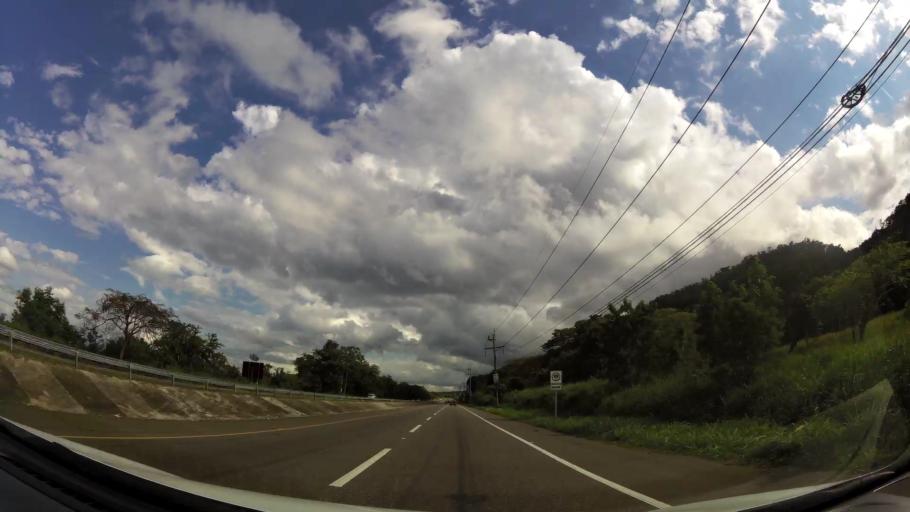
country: DO
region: La Vega
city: Concepcion de La Vega
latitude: 19.1747
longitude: -70.4934
